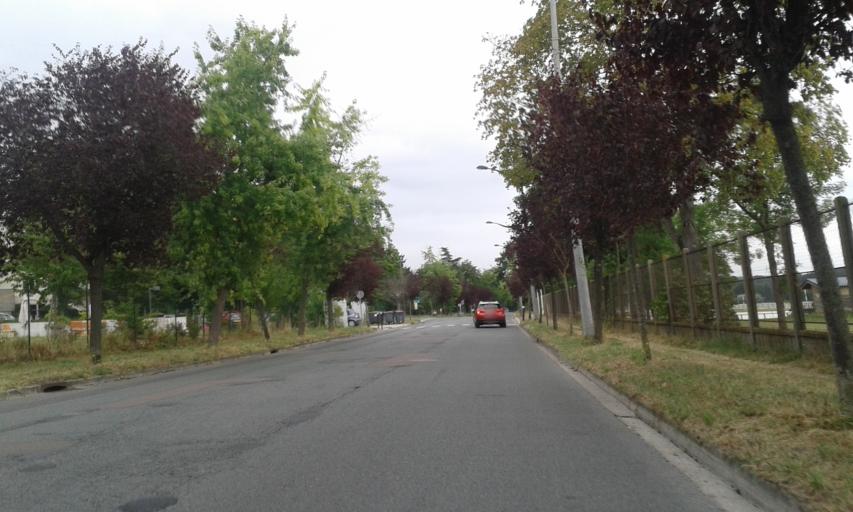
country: FR
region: Ile-de-France
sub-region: Departement des Yvelines
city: Maisons-Laffitte
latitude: 48.9516
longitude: 2.1620
